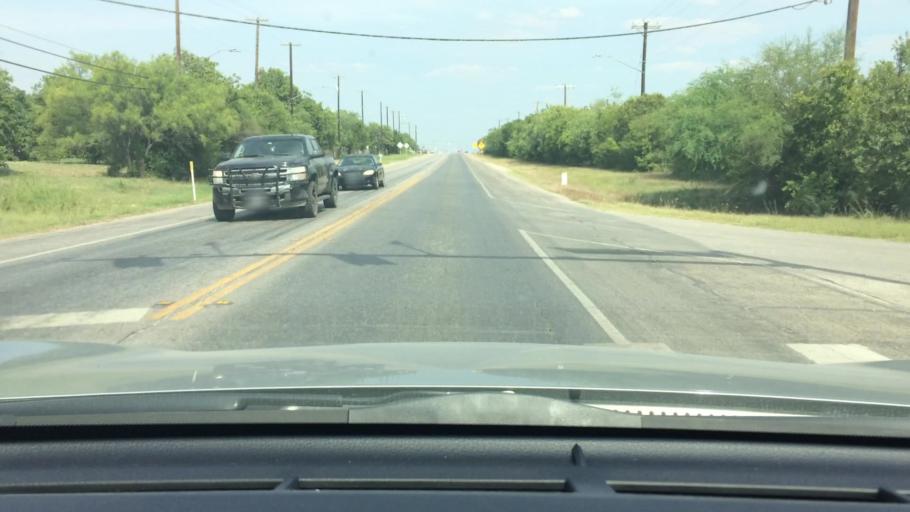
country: US
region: Texas
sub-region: Bexar County
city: China Grove
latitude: 29.3265
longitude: -98.4329
